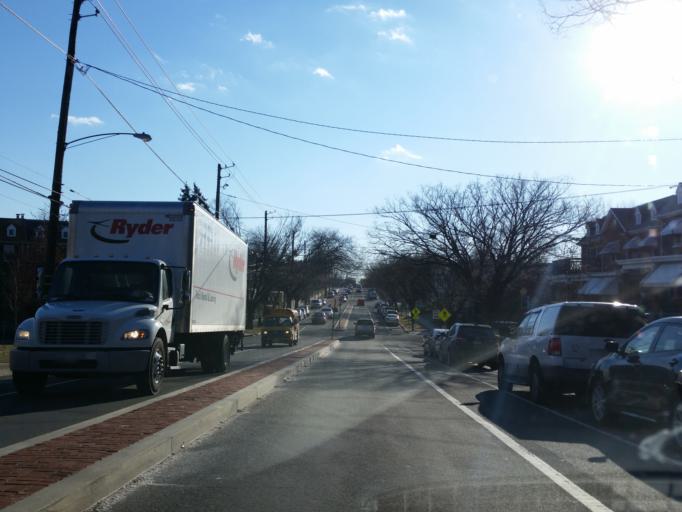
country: US
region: Maryland
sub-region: Montgomery County
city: Takoma Park
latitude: 38.9582
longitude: -77.0138
